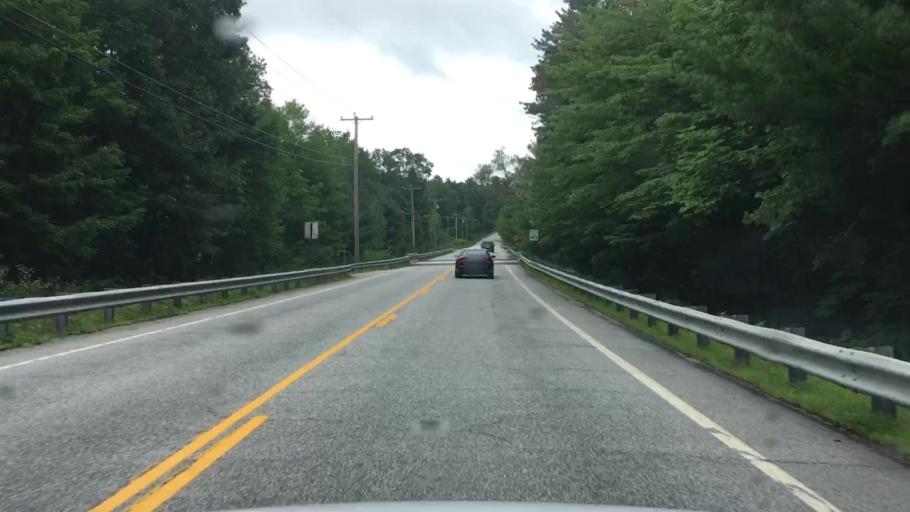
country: US
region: Maine
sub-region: Oxford County
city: Hiram
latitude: 43.8444
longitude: -70.7842
